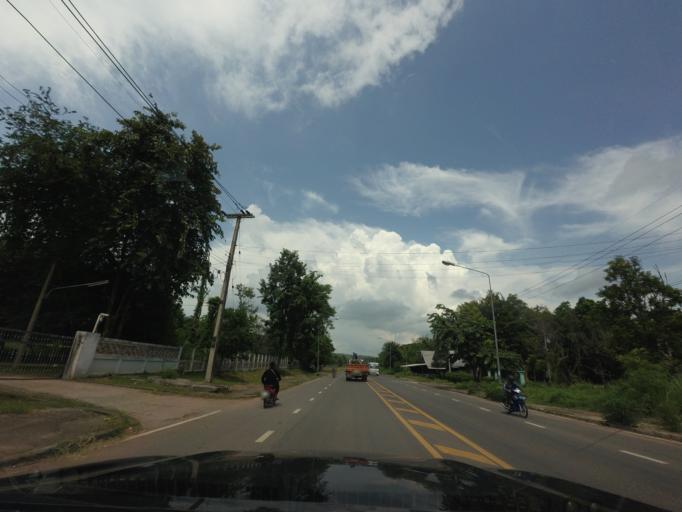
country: TH
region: Khon Kaen
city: Phu Wiang
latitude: 16.6604
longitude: 102.3679
